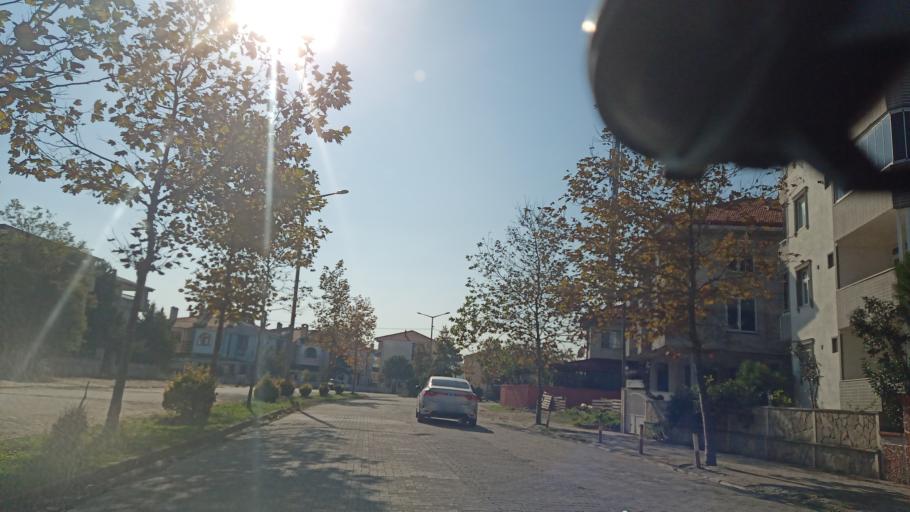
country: TR
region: Sakarya
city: Karasu
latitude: 41.0903
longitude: 30.7420
